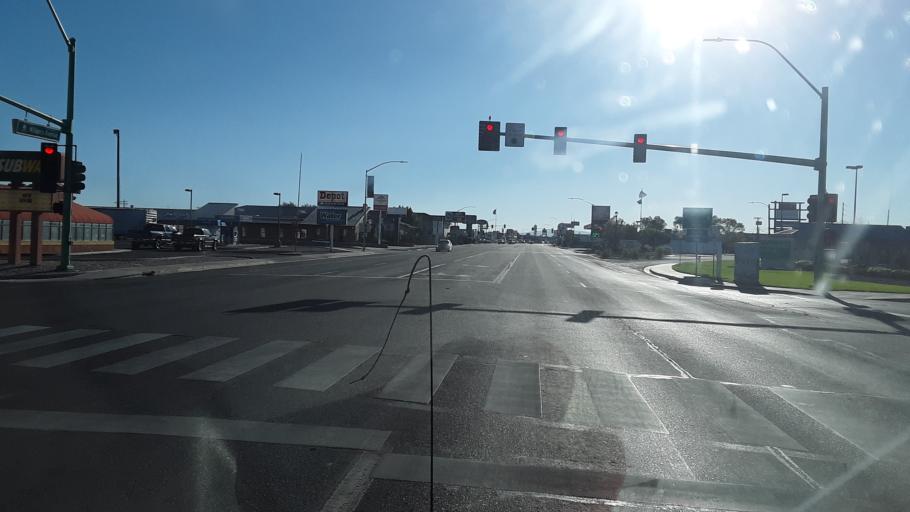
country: US
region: Nevada
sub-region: Churchill County
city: Fallon
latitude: 39.4749
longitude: -118.7877
